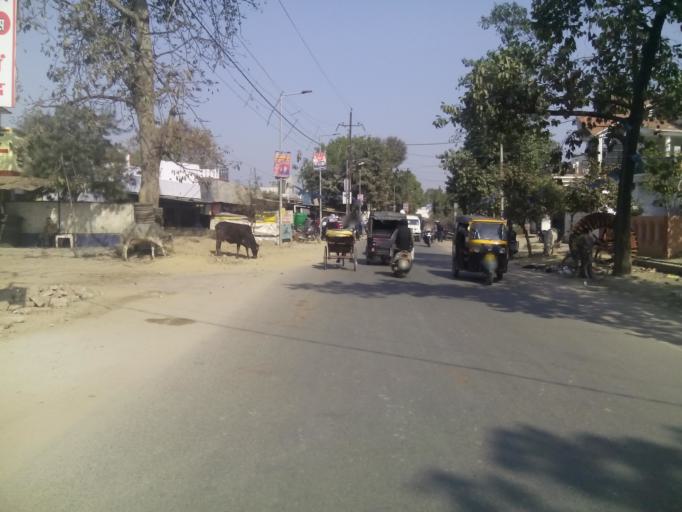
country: IN
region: Uttar Pradesh
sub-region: Bahraich
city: Bahraich
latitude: 27.5664
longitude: 81.5975
